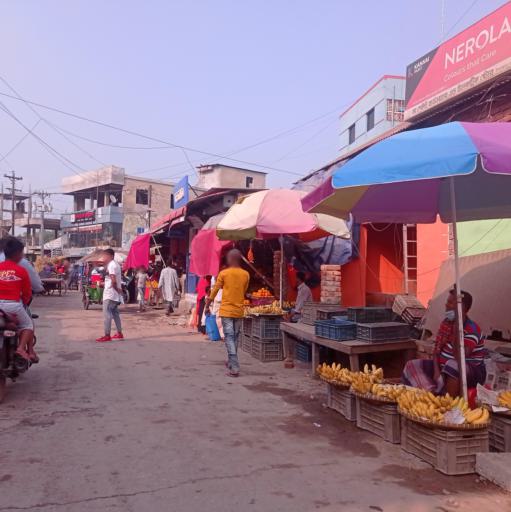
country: BD
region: Dhaka
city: Bhairab Bazar
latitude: 24.1049
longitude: 90.8515
